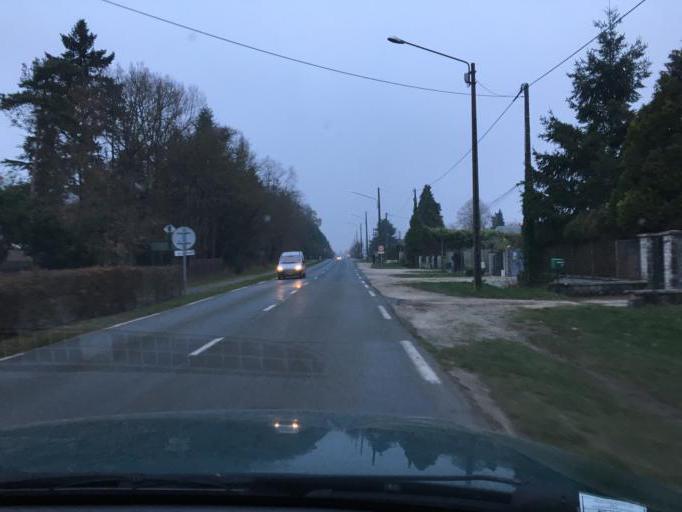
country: FR
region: Centre
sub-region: Departement du Loiret
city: Lailly-en-Val
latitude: 47.7635
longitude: 1.6822
